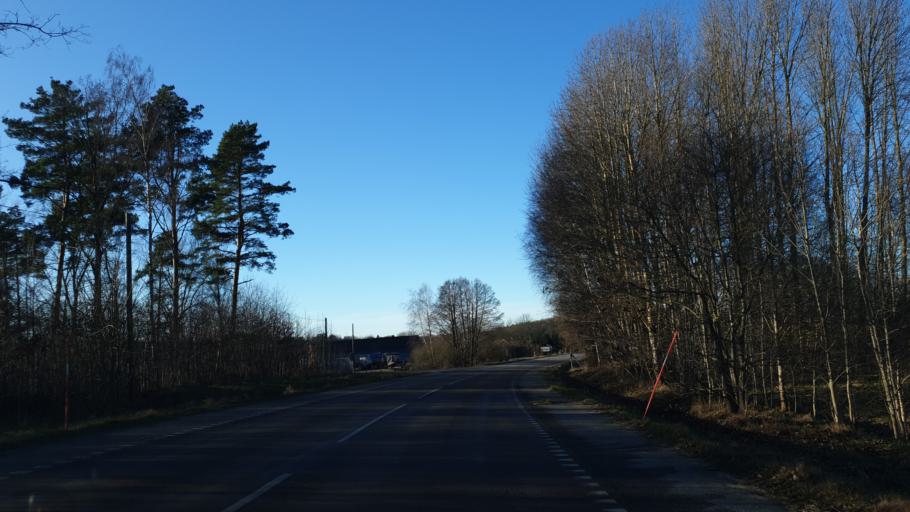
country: SE
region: Blekinge
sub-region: Ronneby Kommun
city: Ronneby
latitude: 56.1919
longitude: 15.3570
